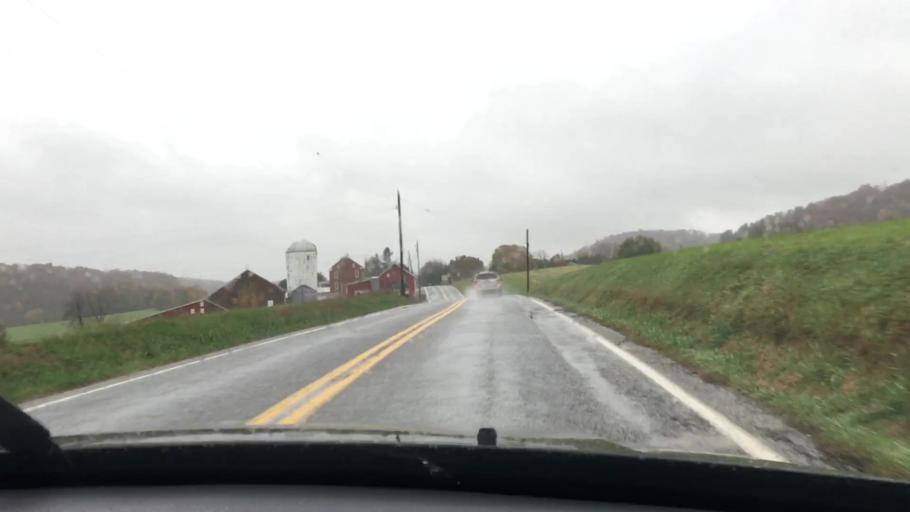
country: US
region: Maryland
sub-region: Carroll County
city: Manchester
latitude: 39.7227
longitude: -76.8385
